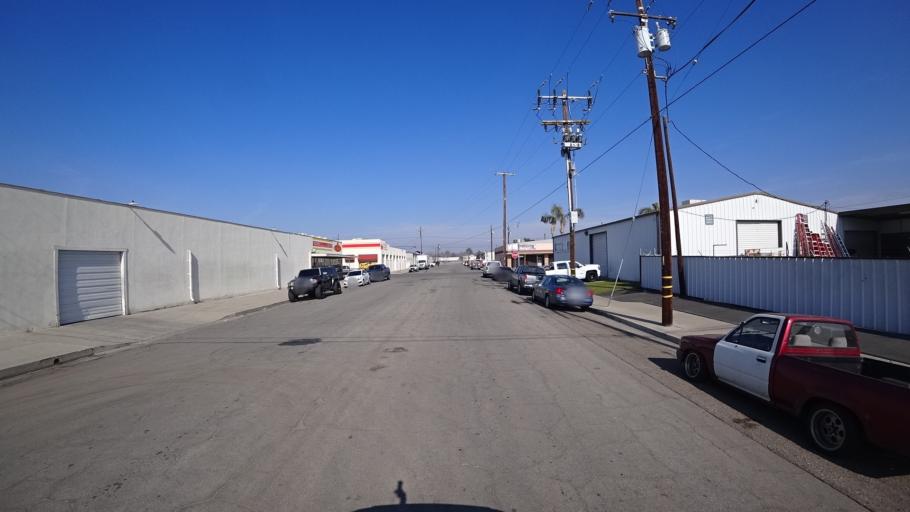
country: US
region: California
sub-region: Kern County
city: Bakersfield
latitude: 35.3750
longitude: -118.9969
